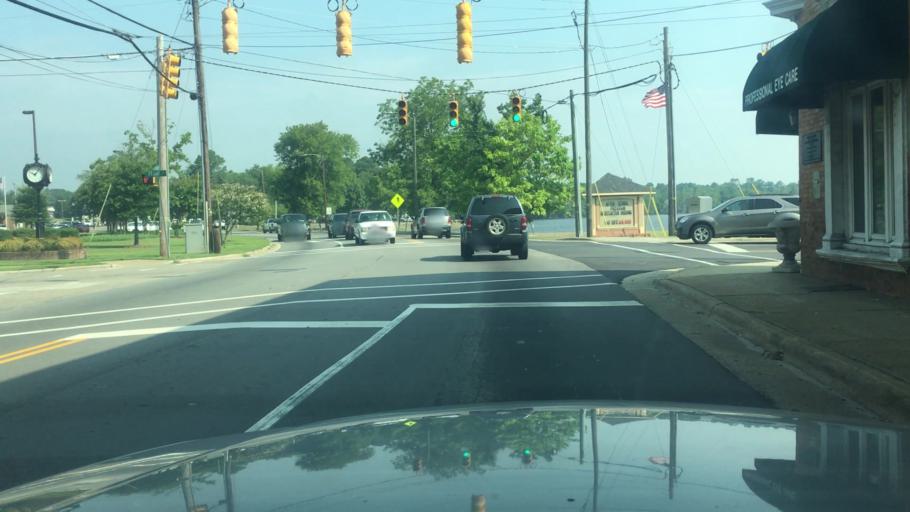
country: US
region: North Carolina
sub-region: Cumberland County
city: Hope Mills
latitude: 34.9719
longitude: -78.9459
